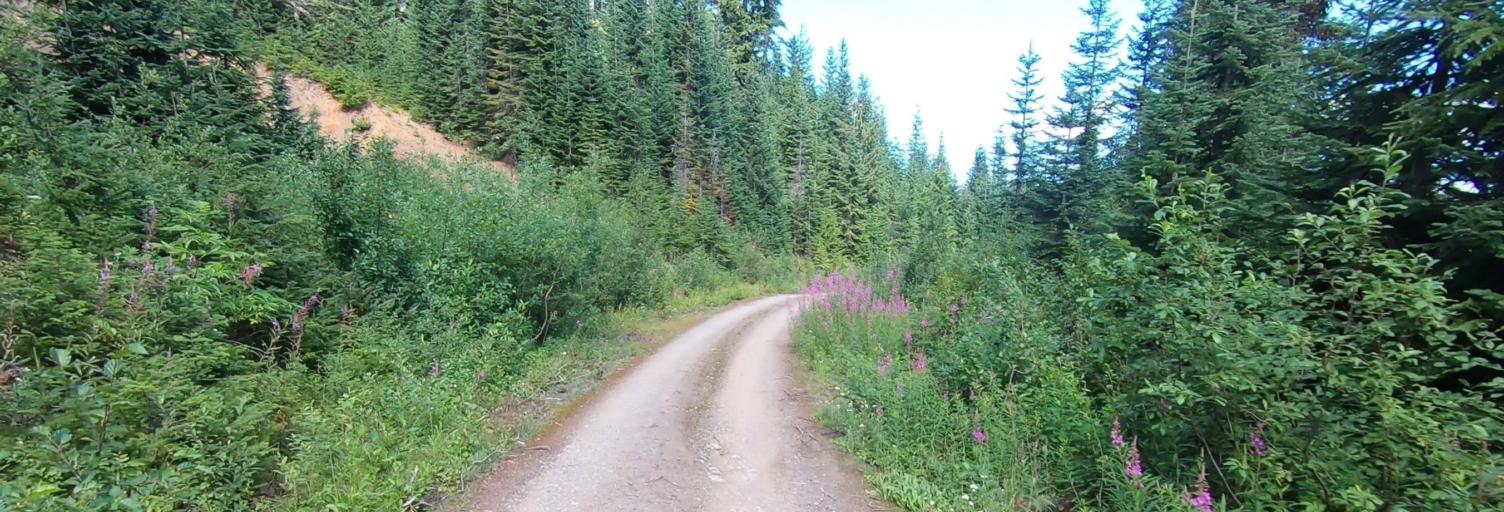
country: CA
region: British Columbia
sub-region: Fraser Valley Regional District
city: Chilliwack
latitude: 48.8745
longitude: -121.8000
